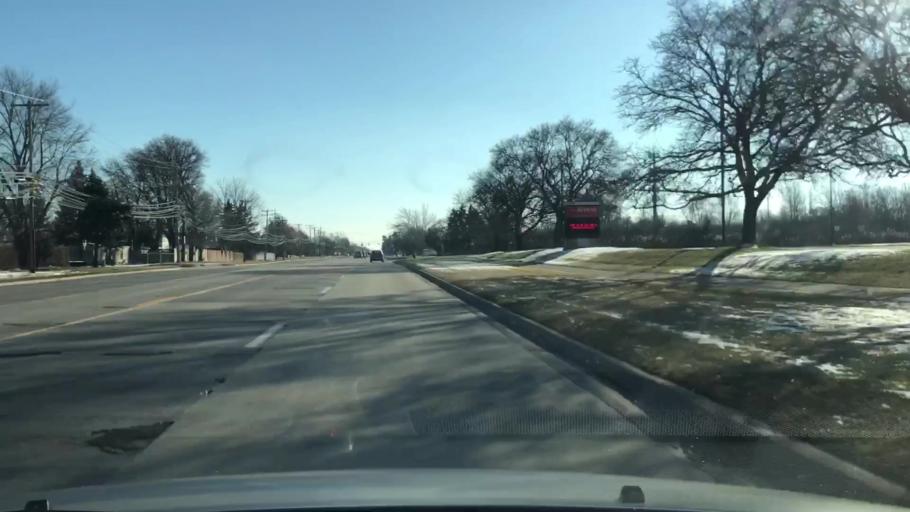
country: US
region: Michigan
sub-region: Oakland County
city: Troy
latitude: 42.5819
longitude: -83.1091
